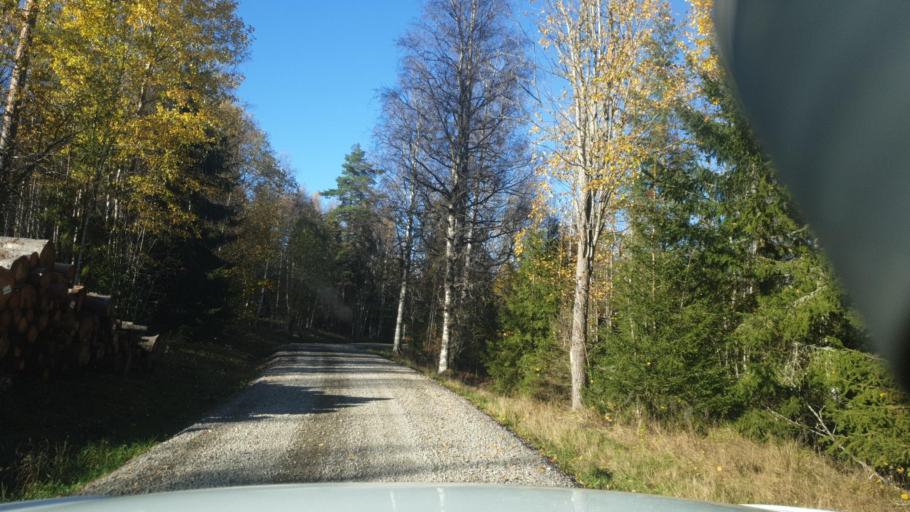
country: SE
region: Vaermland
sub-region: Arvika Kommun
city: Arvika
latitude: 59.5741
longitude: 12.8312
